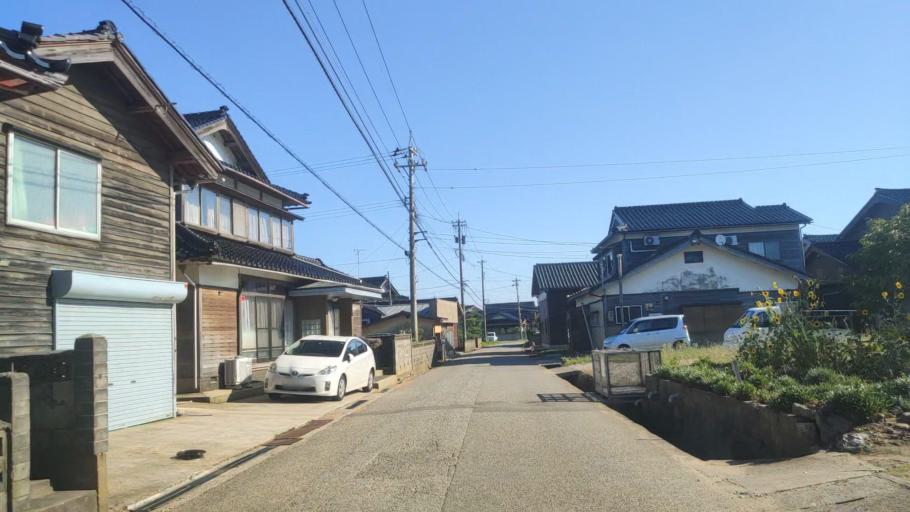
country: JP
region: Ishikawa
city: Hakui
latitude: 36.9512
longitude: 136.7645
